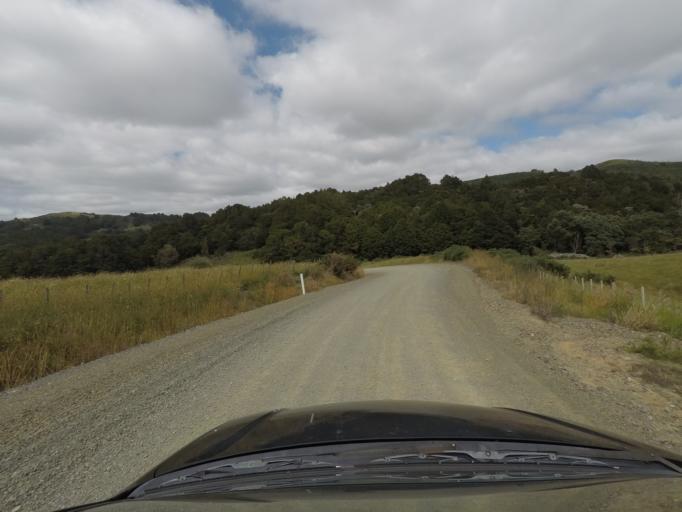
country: NZ
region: Northland
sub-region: Whangarei
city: Ruakaka
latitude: -35.9313
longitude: 174.3459
